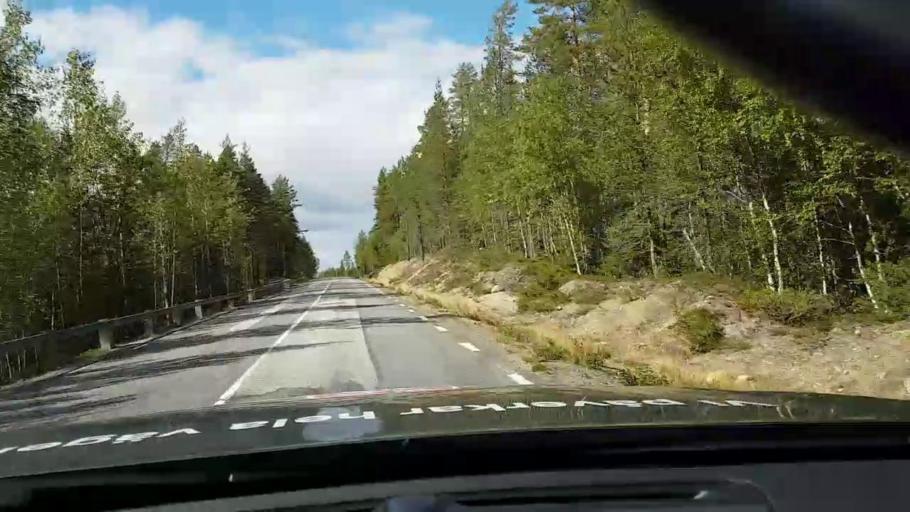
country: SE
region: Vaesterbotten
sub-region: Asele Kommun
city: Asele
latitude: 63.8404
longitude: 17.4295
